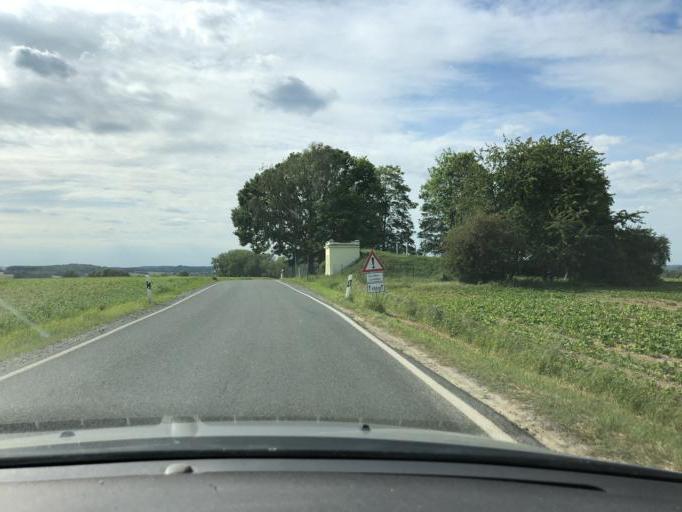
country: DE
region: Saxony
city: Nerchau
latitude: 51.2580
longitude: 12.8009
